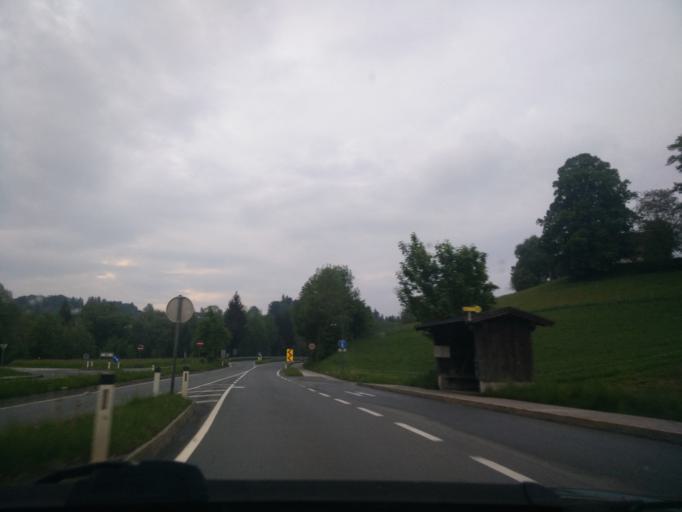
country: AT
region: Salzburg
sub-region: Politischer Bezirk Salzburg-Umgebung
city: Eugendorf
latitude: 47.8784
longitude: 13.1216
